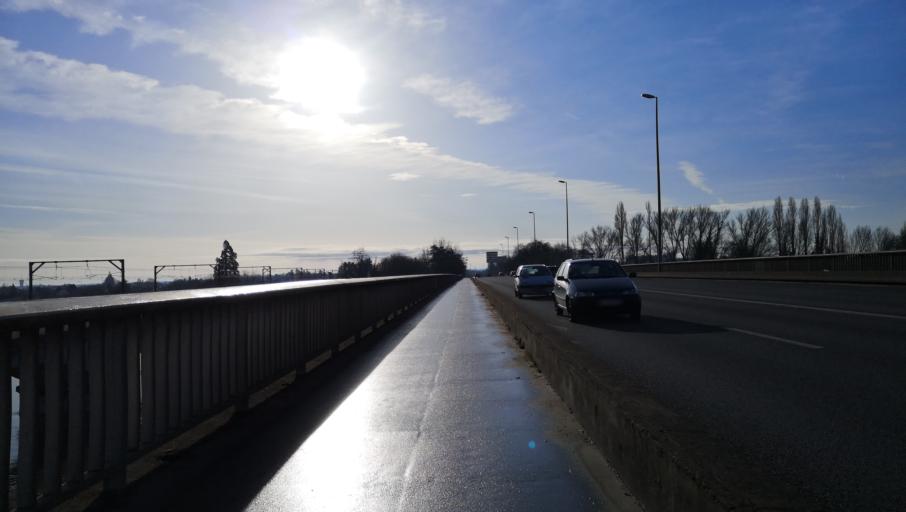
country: FR
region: Centre
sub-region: Departement du Loiret
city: Saint-Jean-le-Blanc
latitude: 47.8971
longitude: 1.9209
